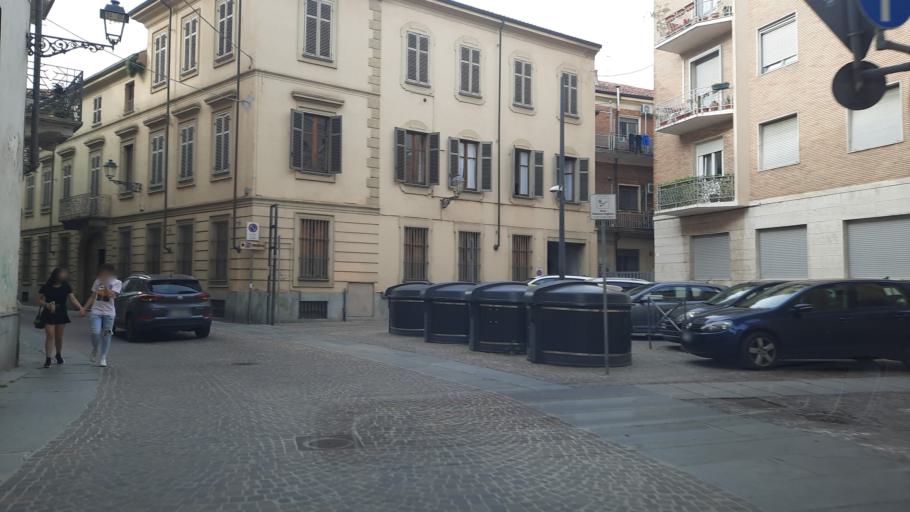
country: IT
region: Piedmont
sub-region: Provincia di Alessandria
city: Casale Monferrato
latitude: 45.1374
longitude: 8.4539
